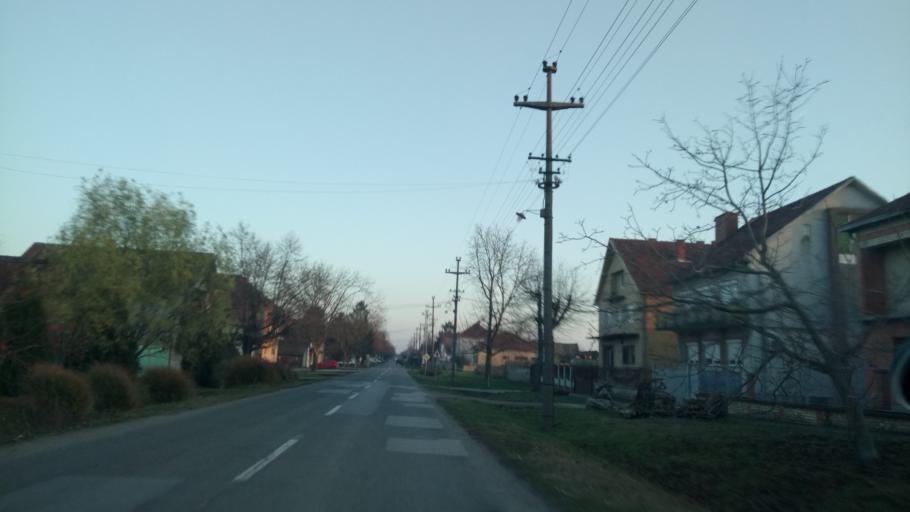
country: RS
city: Surduk
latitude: 45.0765
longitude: 20.3174
